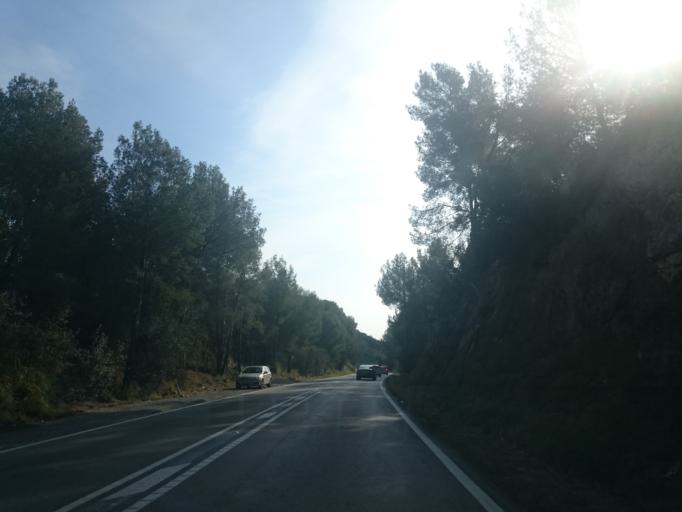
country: ES
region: Catalonia
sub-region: Provincia de Barcelona
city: Gava
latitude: 41.3127
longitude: 1.9704
